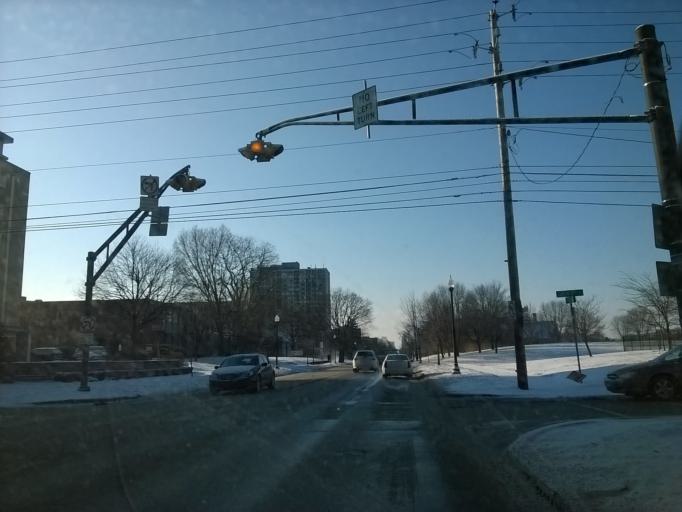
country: US
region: Indiana
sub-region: Marion County
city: Broad Ripple
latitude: 39.8285
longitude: -86.1570
